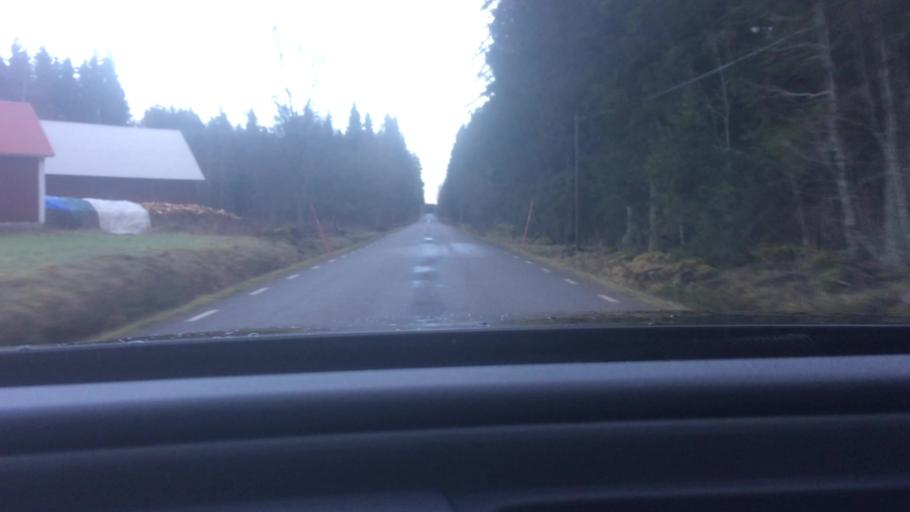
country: SE
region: Vaestra Goetaland
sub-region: Falkopings Kommun
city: Falkoeping
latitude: 58.0206
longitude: 13.5145
